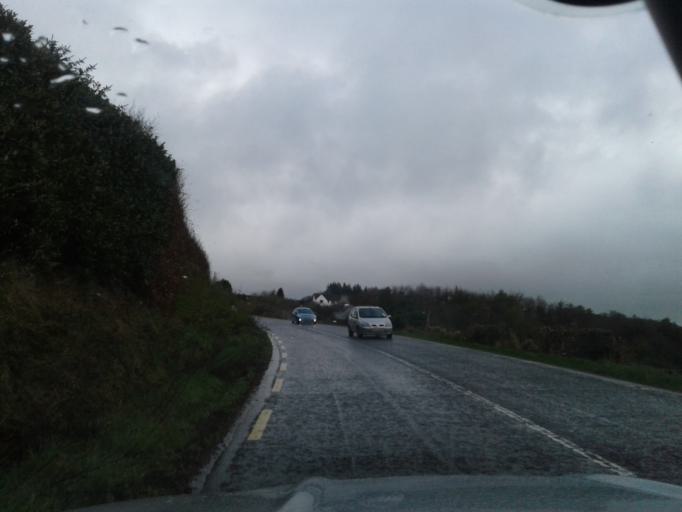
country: IE
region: Ulster
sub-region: County Donegal
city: Letterkenny
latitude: 54.9688
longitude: -7.6893
